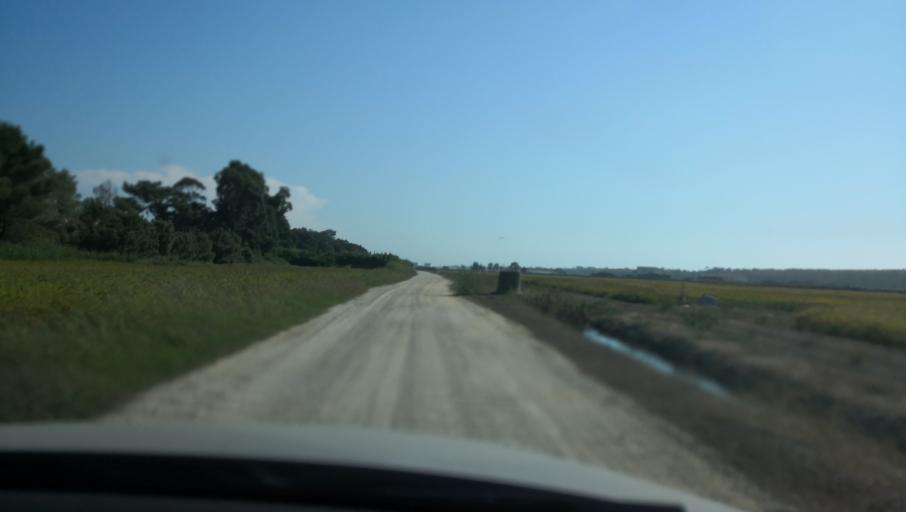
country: PT
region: Setubal
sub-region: Setubal
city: Setubal
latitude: 38.3885
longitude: -8.7897
